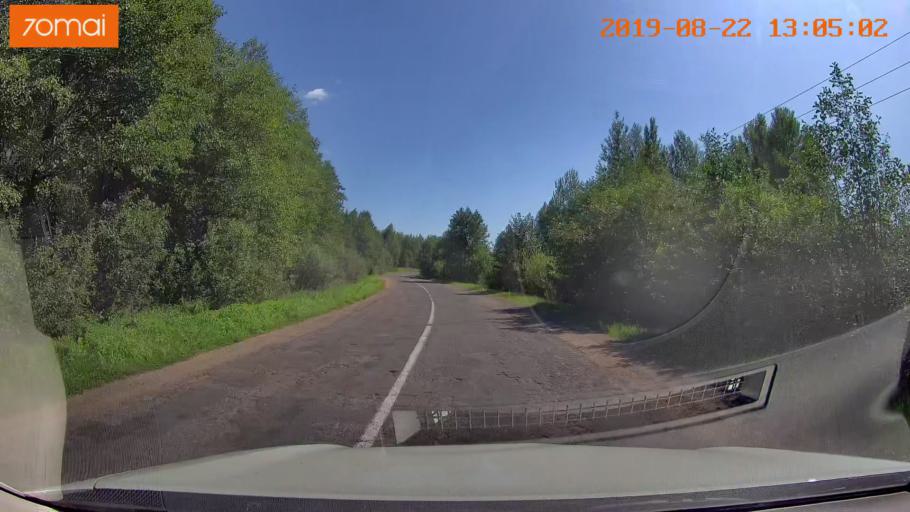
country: BY
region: Minsk
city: Prawdzinski
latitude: 53.3631
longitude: 27.8300
